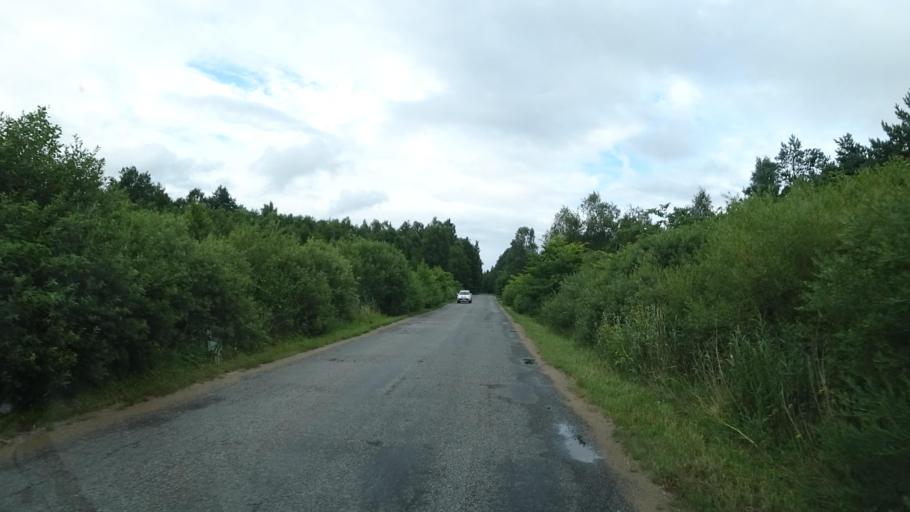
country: LV
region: Liepaja
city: Vec-Liepaja
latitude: 56.6008
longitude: 21.0319
